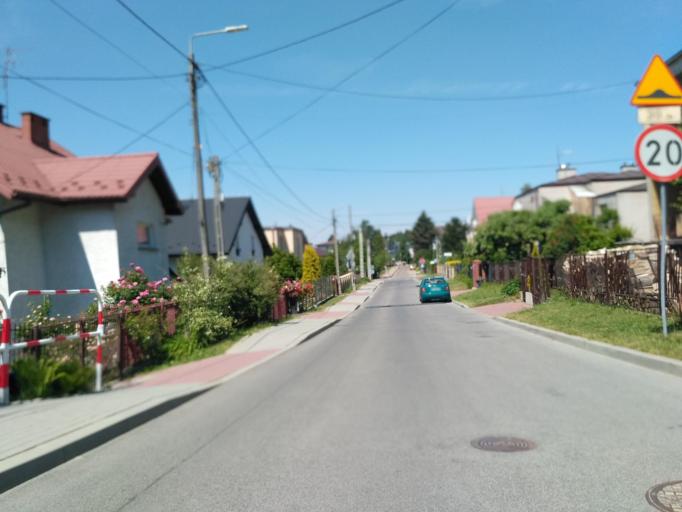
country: PL
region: Subcarpathian Voivodeship
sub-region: Krosno
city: Krosno
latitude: 49.6975
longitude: 21.7736
